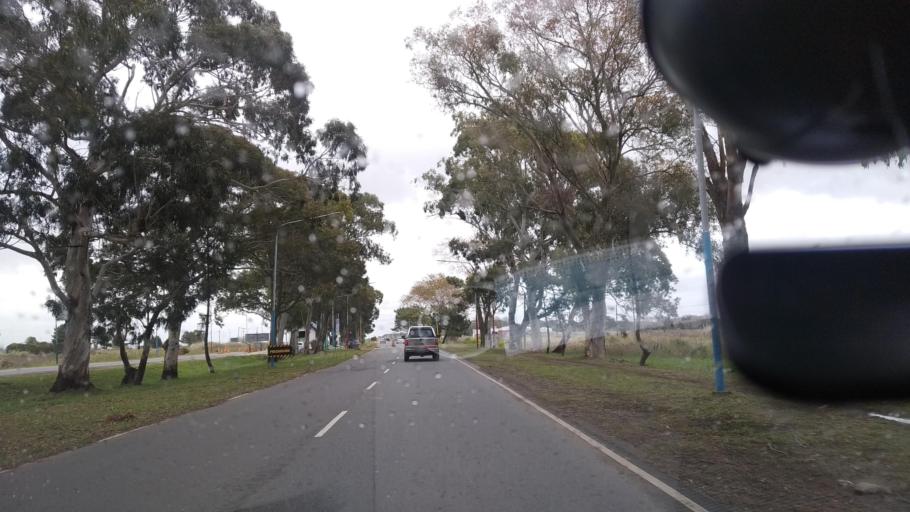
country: AR
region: Buenos Aires
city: San Clemente del Tuyu
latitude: -36.3871
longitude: -56.7331
